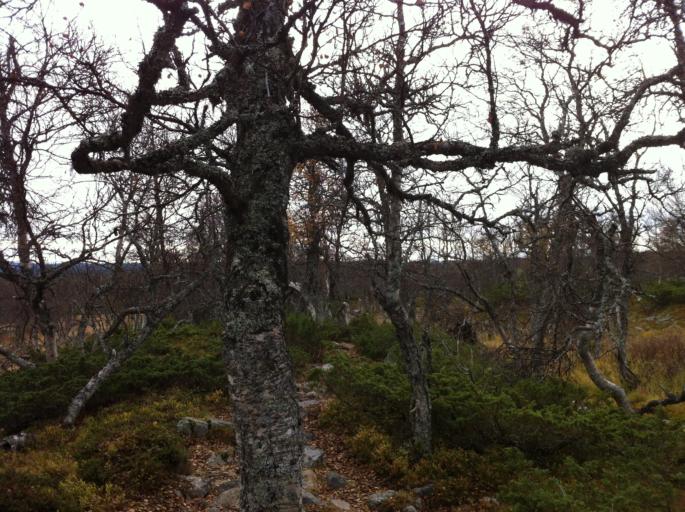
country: NO
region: Hedmark
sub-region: Engerdal
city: Engerdal
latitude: 62.0955
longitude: 12.2652
